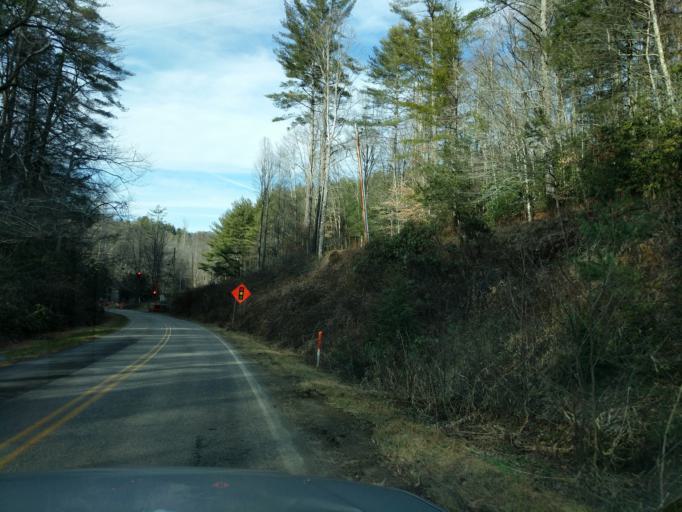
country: US
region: North Carolina
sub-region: Haywood County
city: Cove Creek
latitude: 35.6640
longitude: -83.0124
